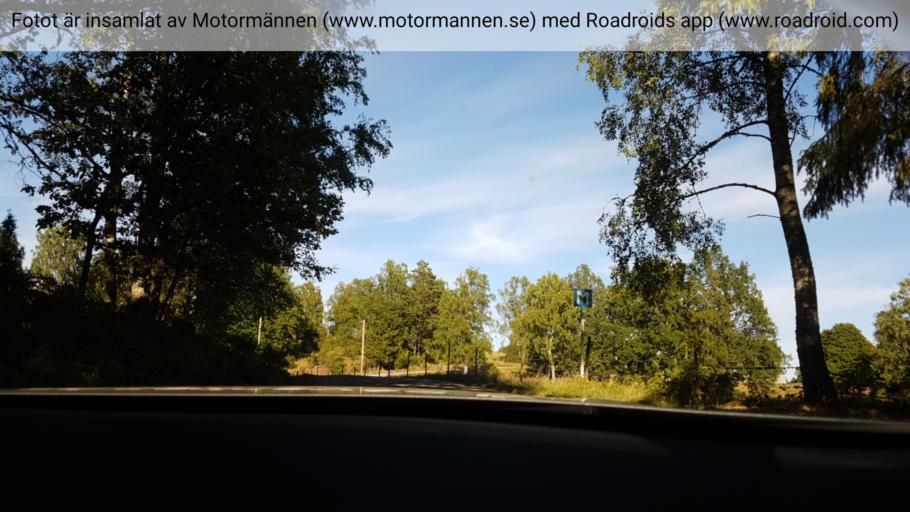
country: SE
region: Joenkoeping
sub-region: Vaggeryds Kommun
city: Skillingaryd
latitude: 57.3810
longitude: 14.0595
